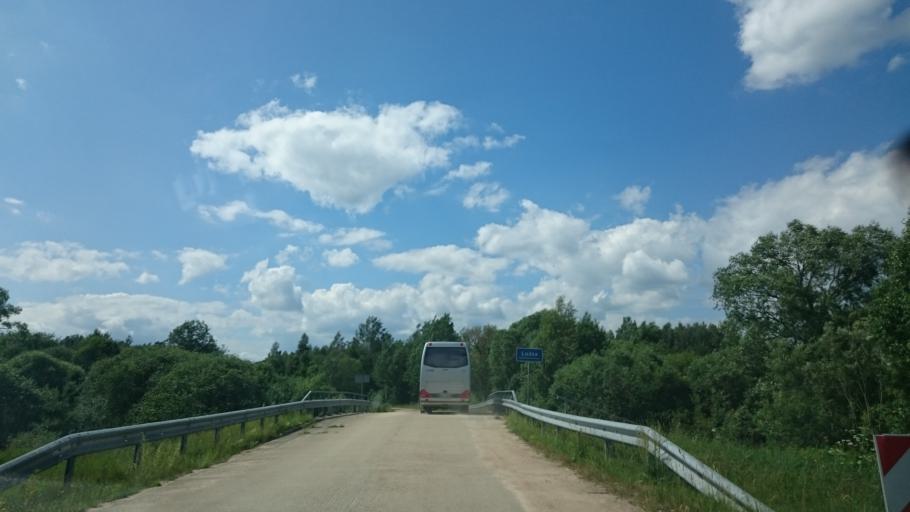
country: LV
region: Cibla
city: Cibla
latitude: 56.6222
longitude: 27.9234
